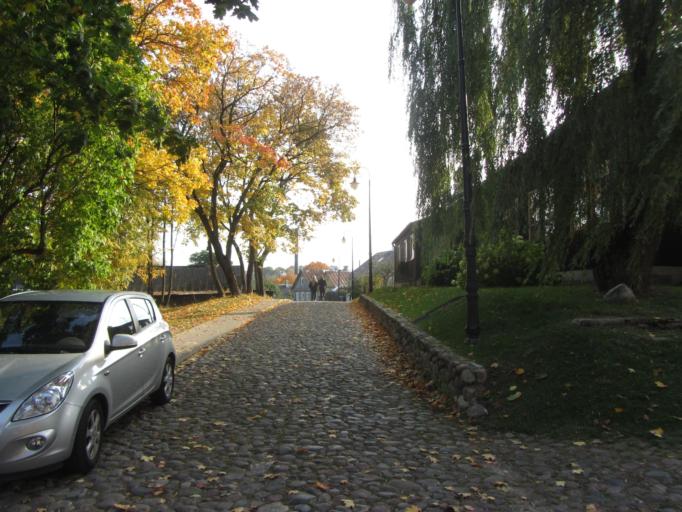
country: LT
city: Trakai
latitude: 54.6426
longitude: 24.9349
